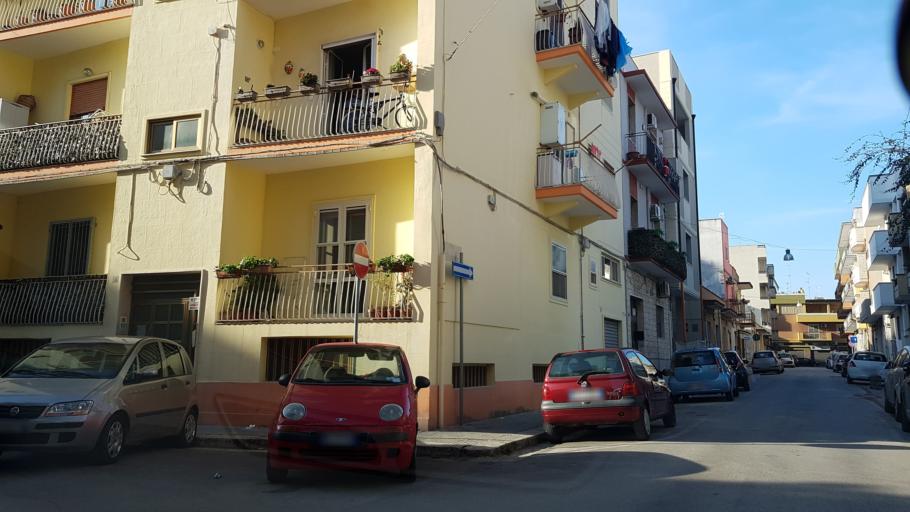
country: IT
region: Apulia
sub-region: Provincia di Brindisi
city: Brindisi
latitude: 40.6343
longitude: 17.9365
